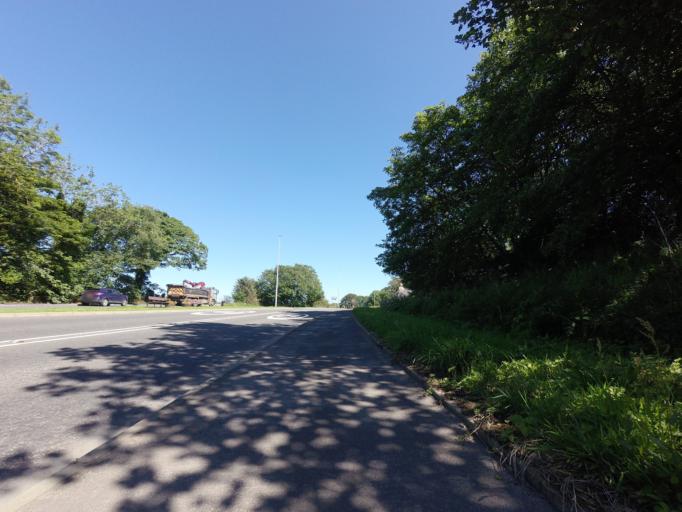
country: GB
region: Scotland
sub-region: Aberdeenshire
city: Macduff
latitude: 57.6610
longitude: -2.4958
